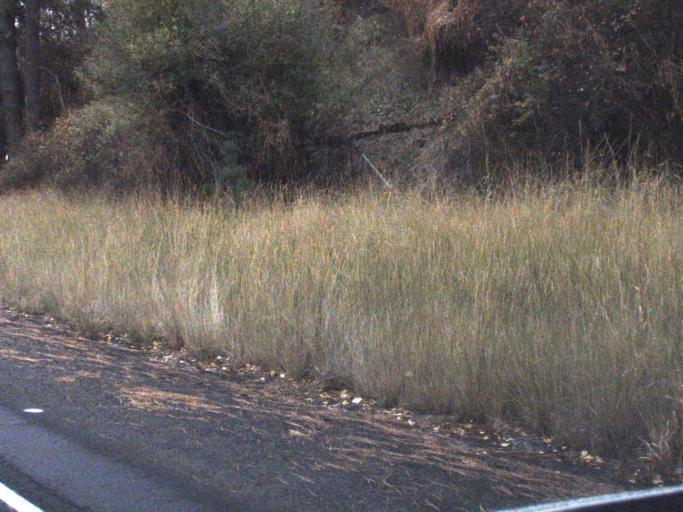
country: US
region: Washington
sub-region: Whitman County
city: Colfax
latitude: 46.8630
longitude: -117.3510
